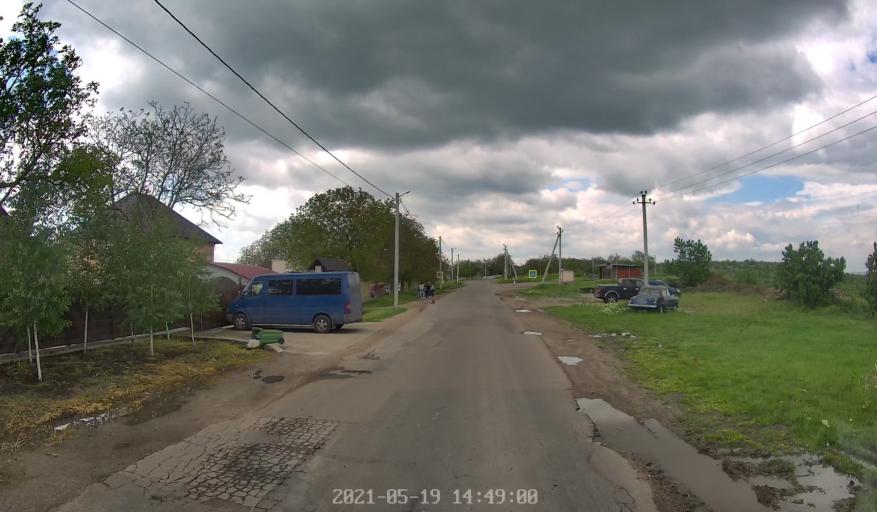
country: MD
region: Chisinau
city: Stauceni
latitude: 47.0471
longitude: 28.9556
